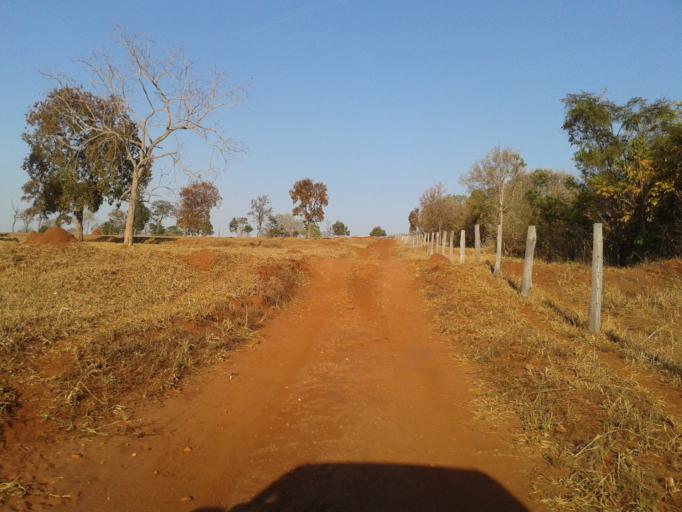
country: BR
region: Minas Gerais
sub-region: Campina Verde
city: Campina Verde
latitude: -19.2611
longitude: -49.6141
